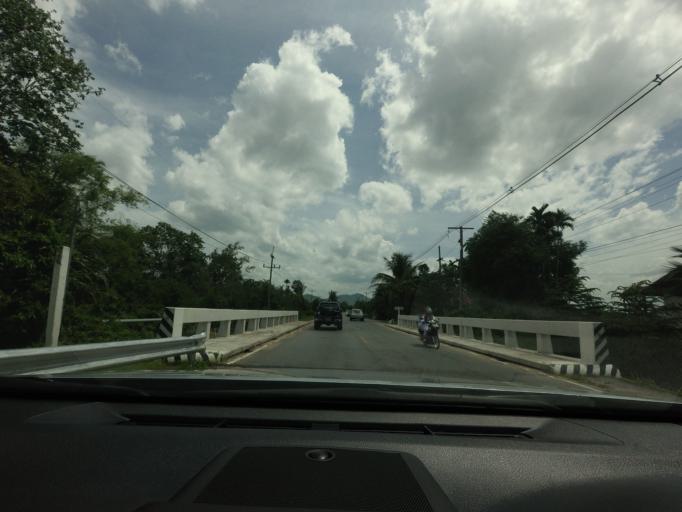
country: TH
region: Yala
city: Raman
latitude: 6.4630
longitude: 101.3764
